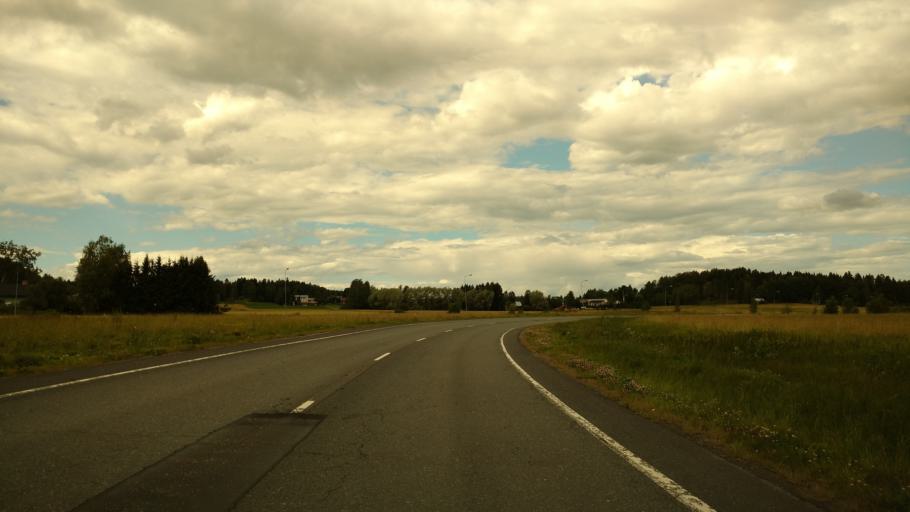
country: FI
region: Varsinais-Suomi
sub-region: Salo
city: Halikko
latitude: 60.3869
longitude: 23.0503
